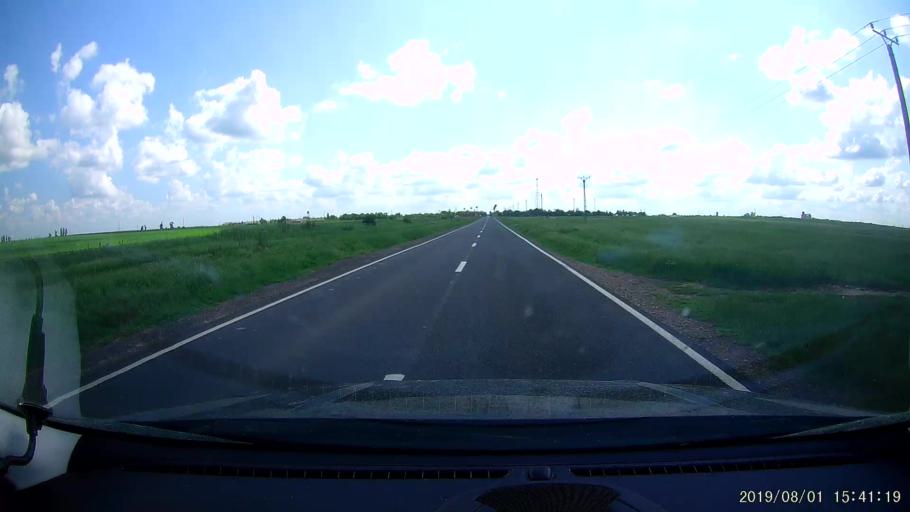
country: RO
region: Braila
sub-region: Comuna Baraganul
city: Baraganul
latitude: 44.8240
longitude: 27.5279
